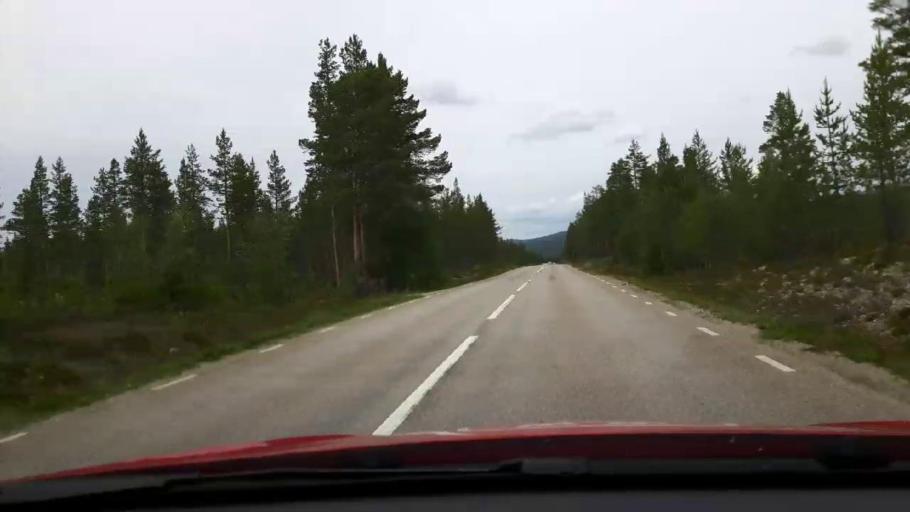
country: SE
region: Jaemtland
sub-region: Harjedalens Kommun
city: Sveg
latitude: 62.2509
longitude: 13.8419
